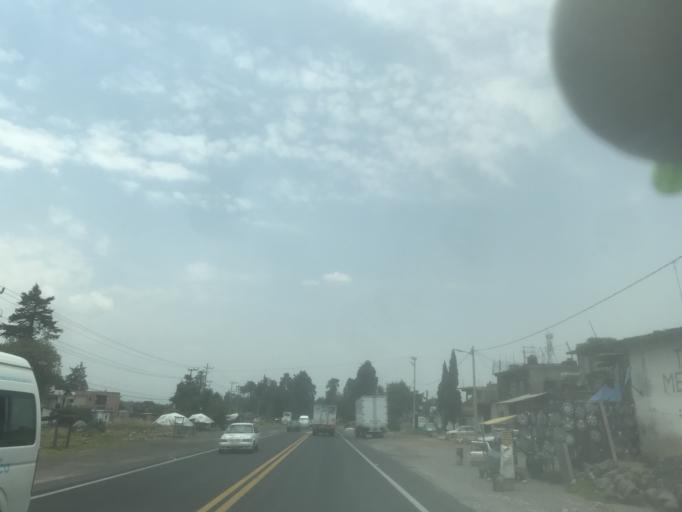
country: MX
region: Mexico
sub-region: Amecameca
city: San Diego Huehuecalco
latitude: 19.0846
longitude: -98.7820
